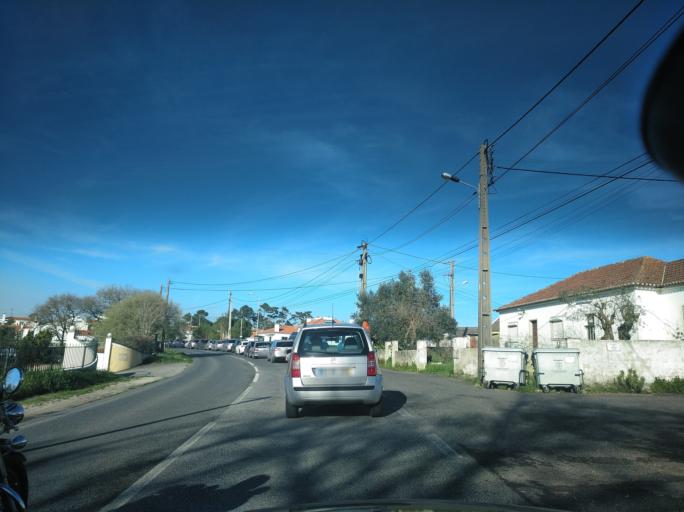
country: PT
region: Lisbon
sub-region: Mafra
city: Mafra
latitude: 38.9293
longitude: -9.3112
